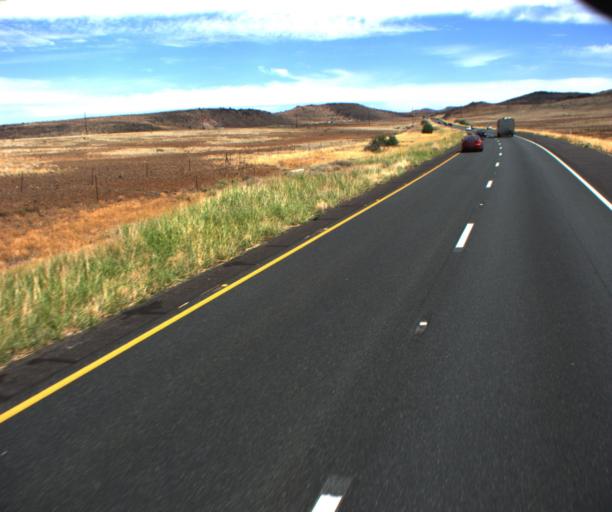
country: US
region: Arizona
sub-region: Yavapai County
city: Cordes Lakes
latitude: 34.4363
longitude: -112.0315
